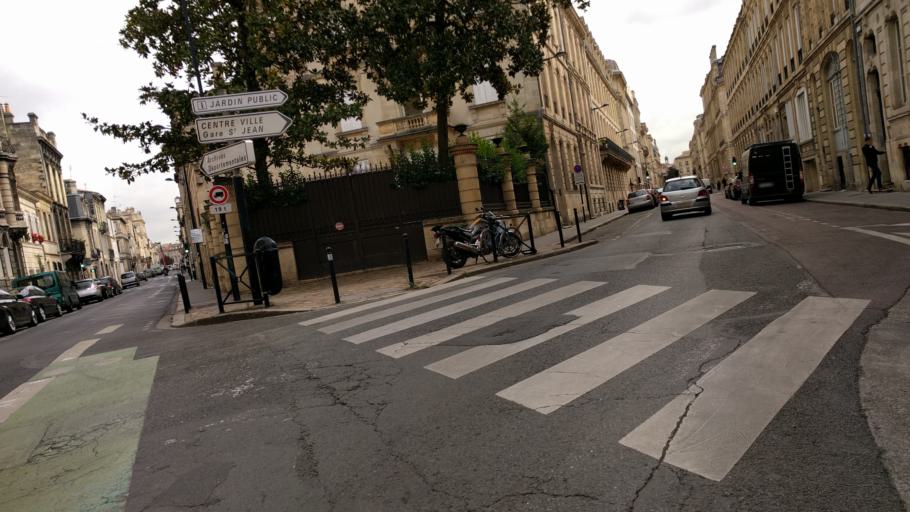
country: FR
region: Aquitaine
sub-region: Departement de la Gironde
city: Bordeaux
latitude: 44.8507
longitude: -0.5788
